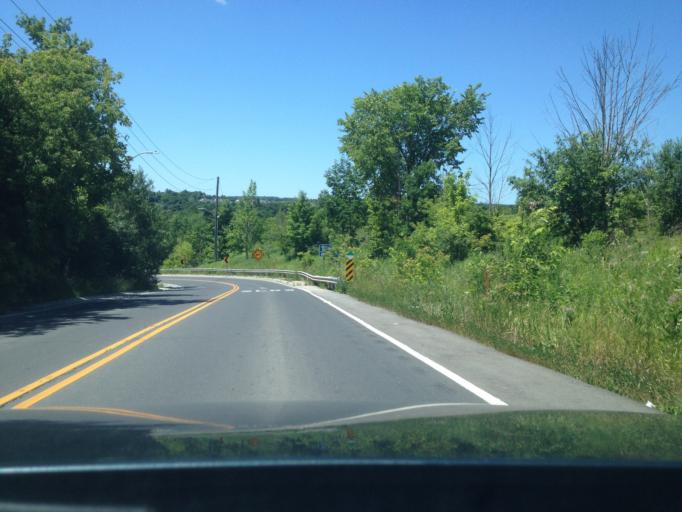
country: CA
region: Ontario
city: Brampton
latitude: 43.6636
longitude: -79.9075
